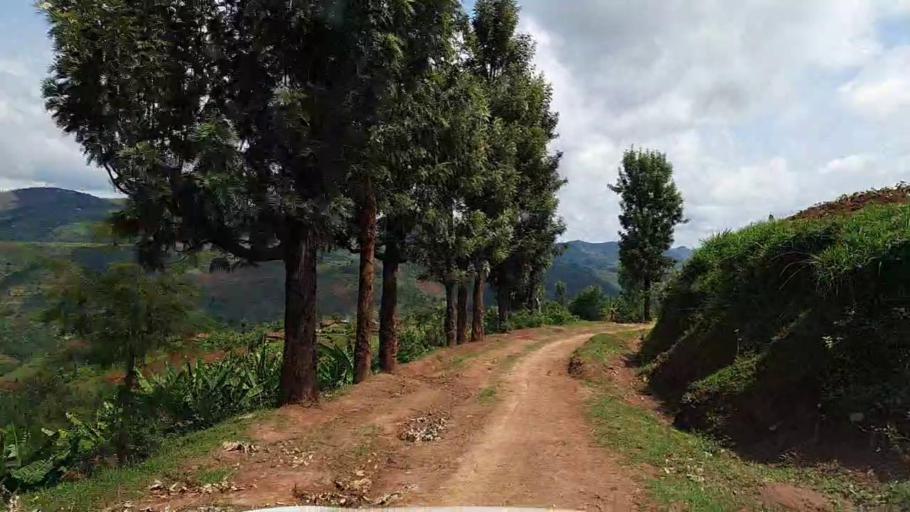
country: RW
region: Southern Province
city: Gikongoro
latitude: -2.3572
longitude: 29.5462
